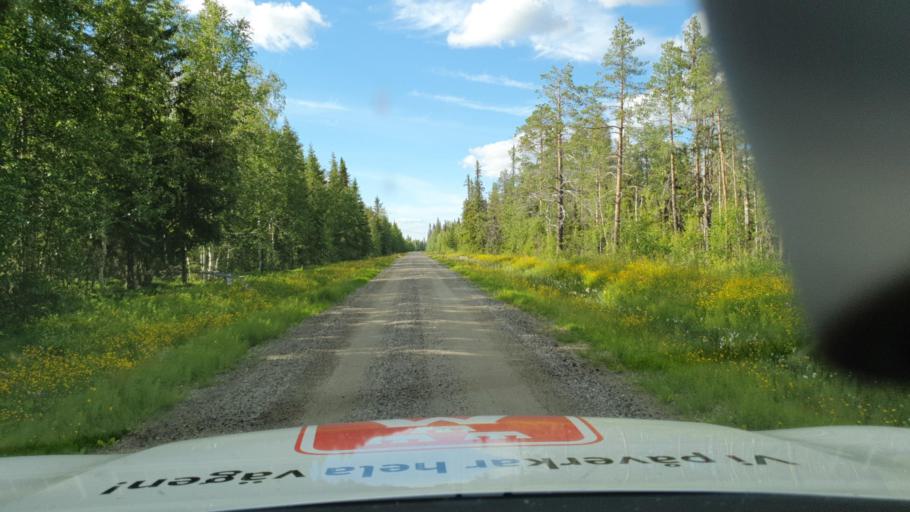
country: SE
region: Vaesterbotten
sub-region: Lycksele Kommun
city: Lycksele
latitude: 64.4349
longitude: 18.2720
